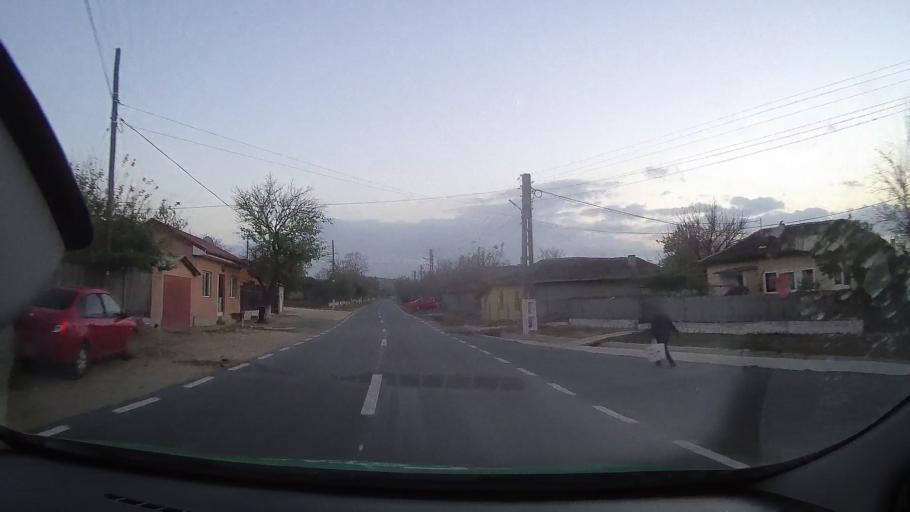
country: RO
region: Constanta
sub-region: Comuna Oltina
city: Oltina
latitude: 44.1622
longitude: 27.6674
